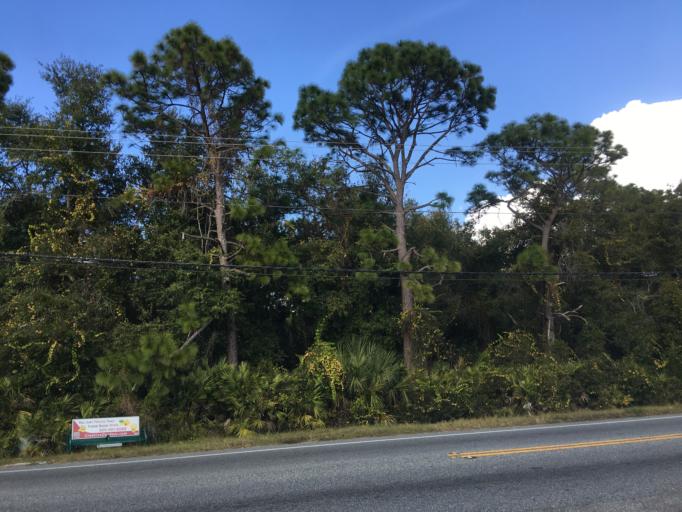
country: US
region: Florida
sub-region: Orange County
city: Eatonville
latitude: 28.6184
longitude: -81.3952
